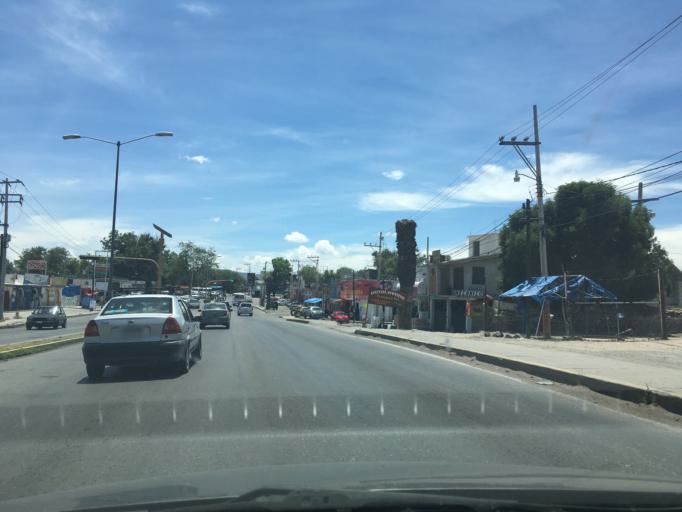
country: MX
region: Hidalgo
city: Ixmiquilpan
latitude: 20.4796
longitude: -99.2288
